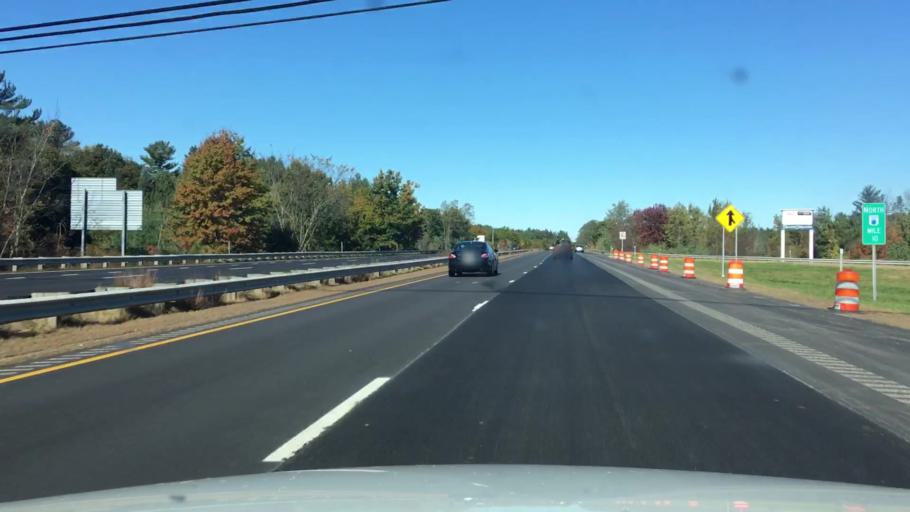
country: US
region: New Hampshire
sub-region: Strafford County
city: Dover
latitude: 43.1876
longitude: -70.8890
